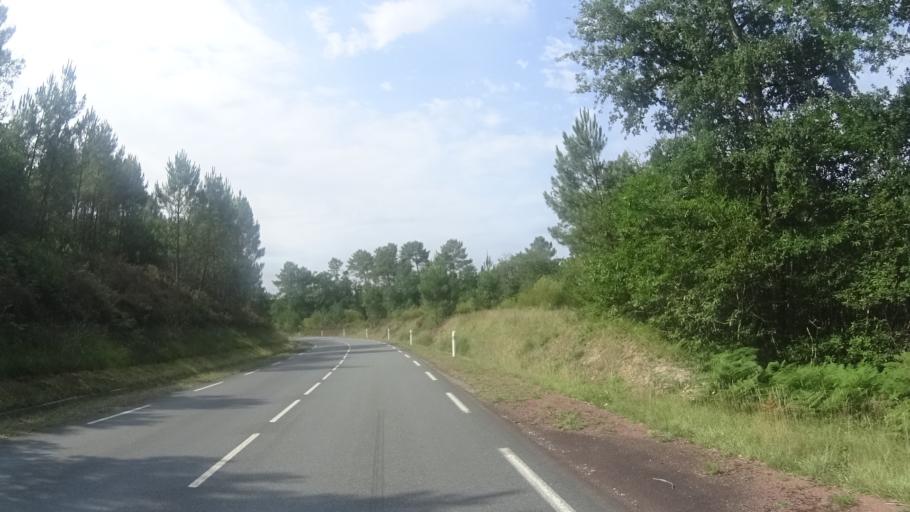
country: FR
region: Aquitaine
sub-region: Departement de la Dordogne
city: Sourzac
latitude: 45.0692
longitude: 0.3714
